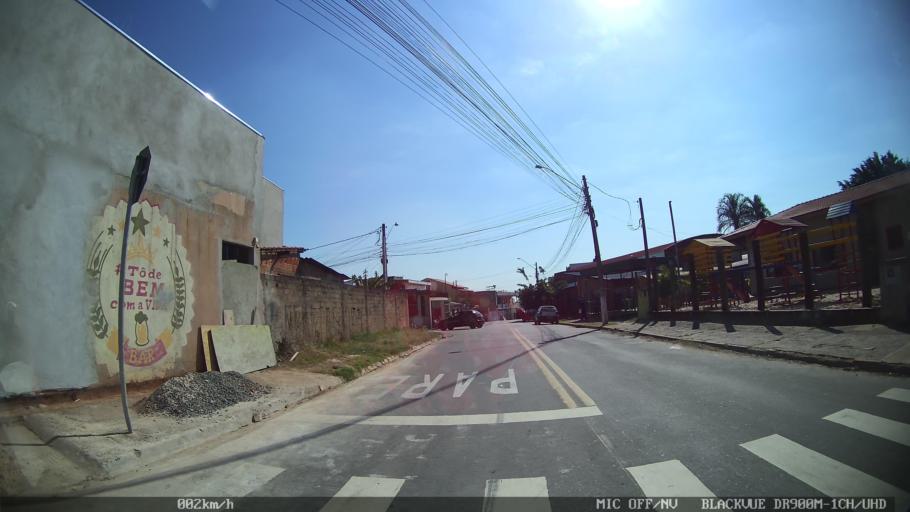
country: BR
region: Sao Paulo
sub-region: Campinas
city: Campinas
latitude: -22.9373
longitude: -47.0774
